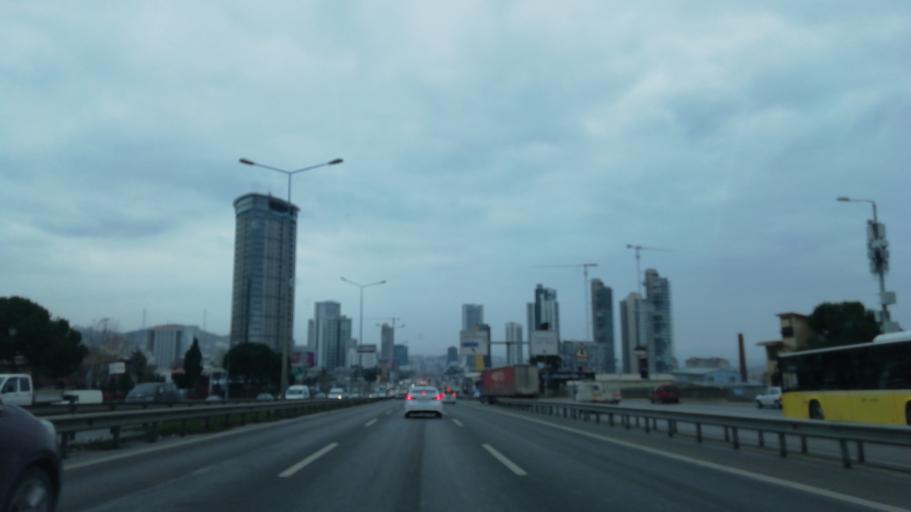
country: TR
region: Istanbul
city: Pendik
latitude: 40.9048
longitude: 29.2131
